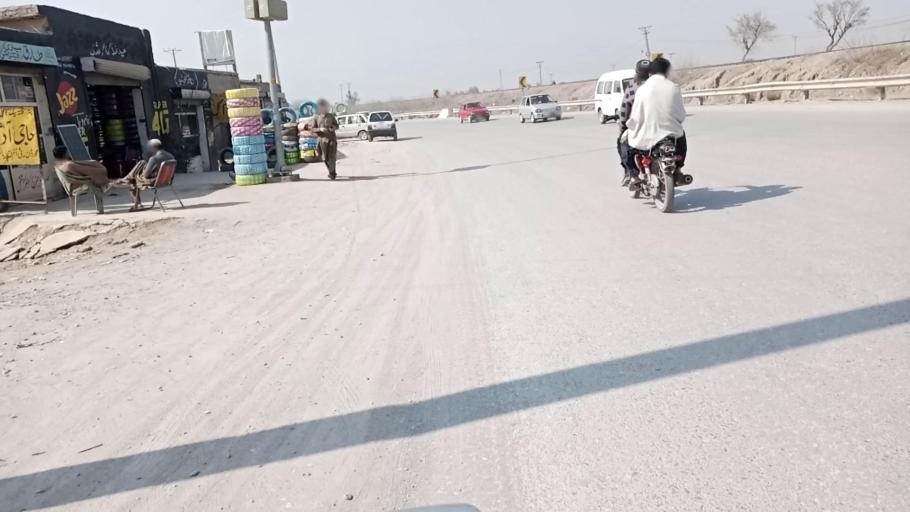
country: PK
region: Khyber Pakhtunkhwa
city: Peshawar
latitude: 34.0014
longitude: 71.3981
